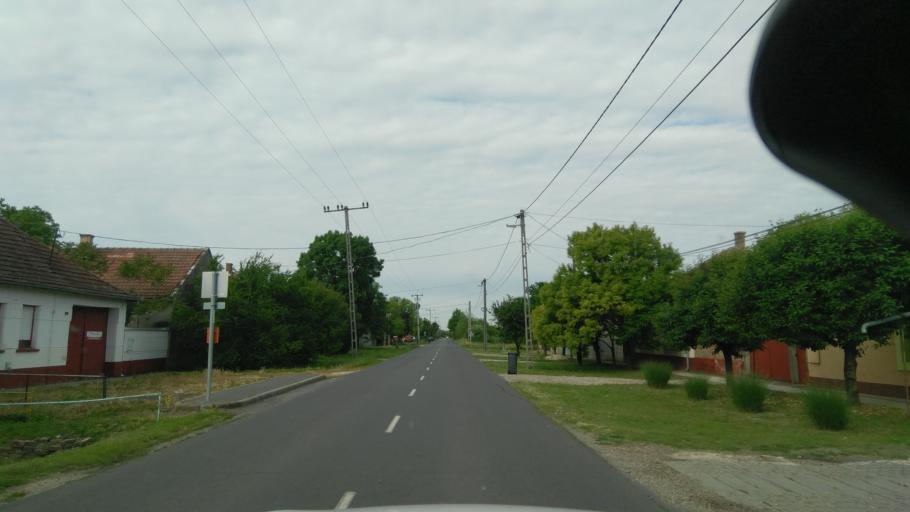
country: HU
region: Bekes
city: Ketegyhaza
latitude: 46.5438
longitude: 21.1751
